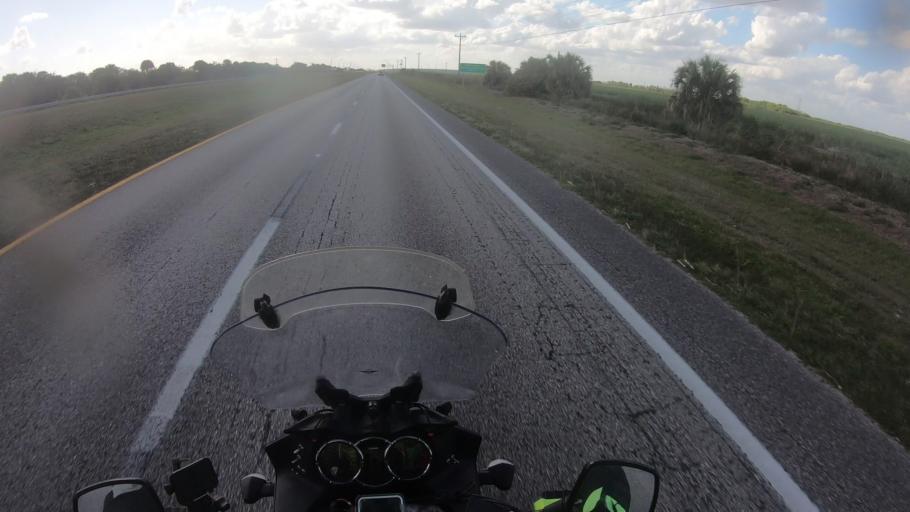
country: US
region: Florida
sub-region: Glades County
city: Moore Haven
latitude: 26.7534
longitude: -81.0691
